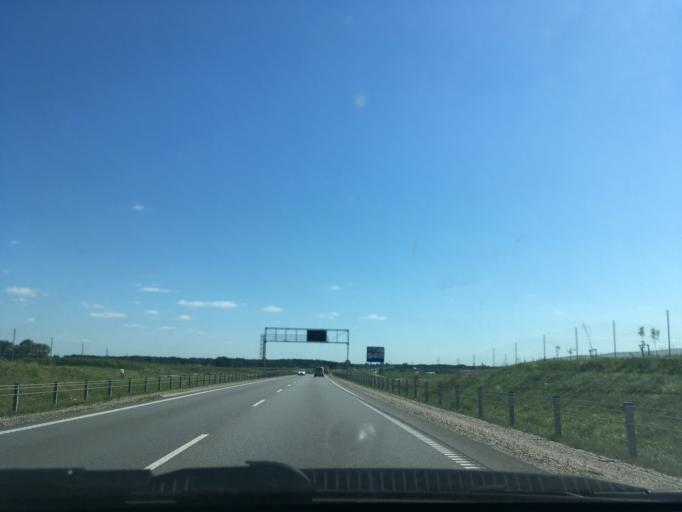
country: PL
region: Podlasie
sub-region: Powiat augustowski
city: Augustow
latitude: 53.8910
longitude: 22.8659
